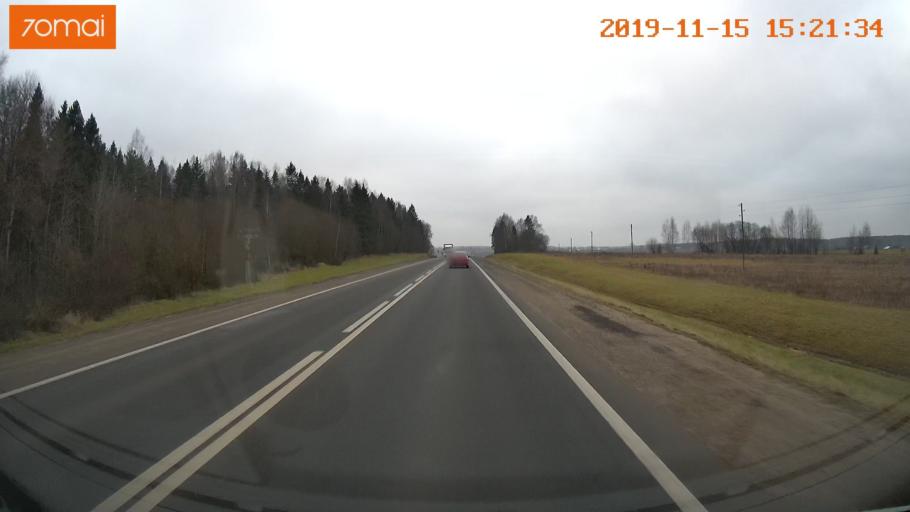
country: RU
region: Jaroslavl
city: Danilov
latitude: 58.2113
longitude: 40.1437
